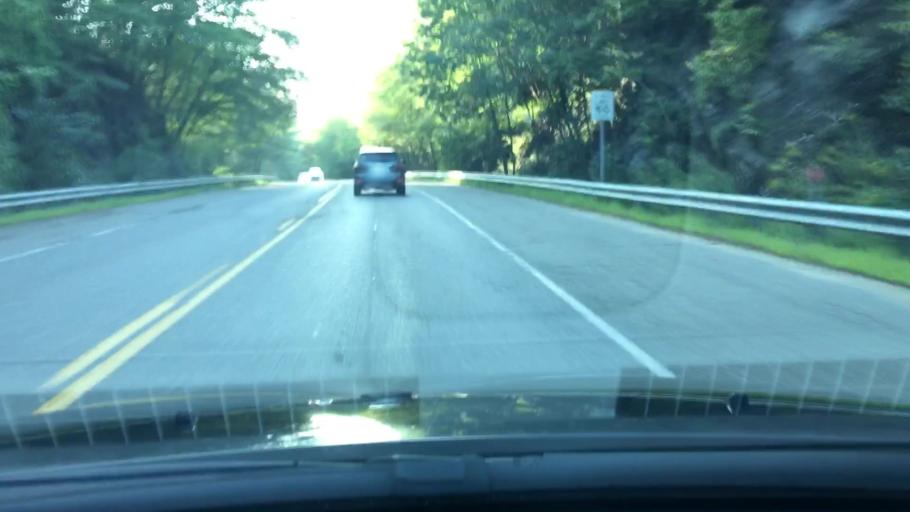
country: US
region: Massachusetts
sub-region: Worcester County
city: West Boylston
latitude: 42.3375
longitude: -71.7493
